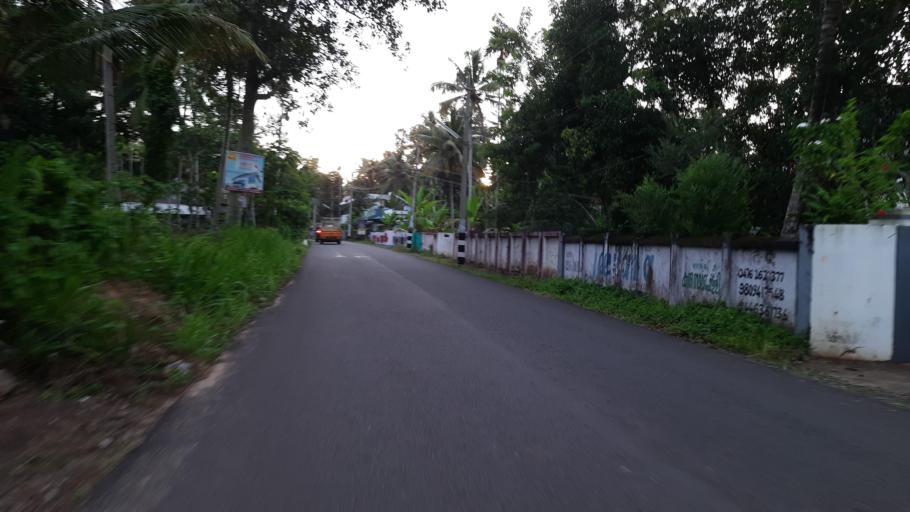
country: IN
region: Kerala
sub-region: Alappuzha
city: Kattanam
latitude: 9.1378
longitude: 76.5467
